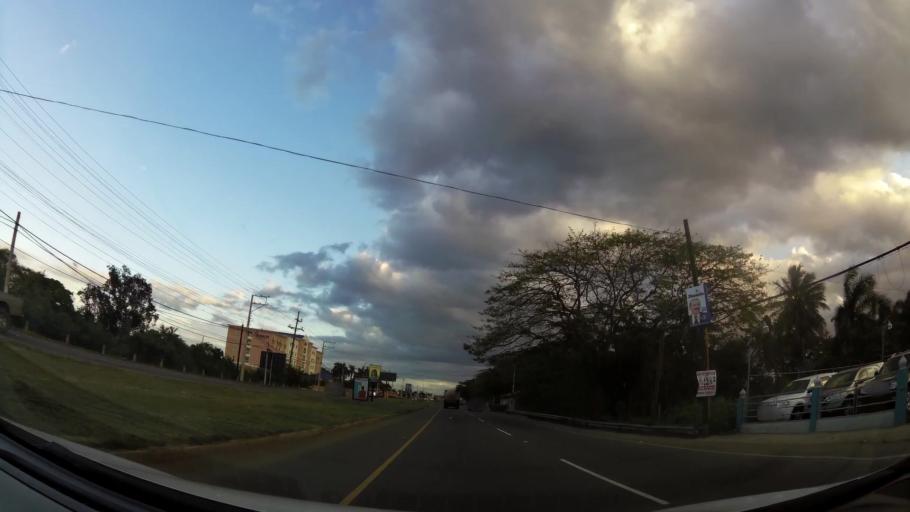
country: DO
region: Santiago
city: Licey al Medio
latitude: 19.4003
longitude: -70.6314
